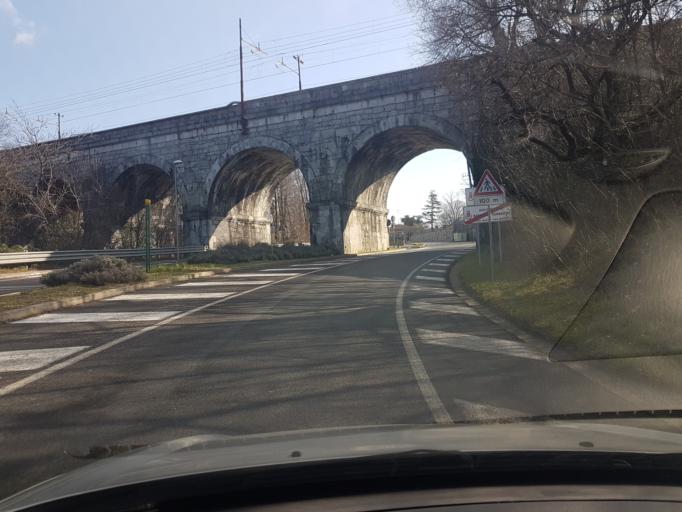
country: IT
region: Friuli Venezia Giulia
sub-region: Provincia di Trieste
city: Aurisina
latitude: 45.7539
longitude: 13.6677
